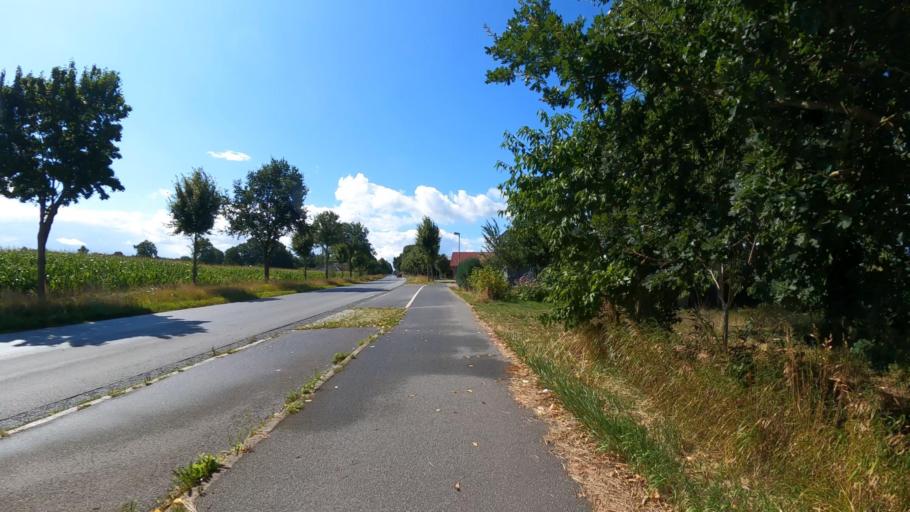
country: DE
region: Schleswig-Holstein
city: Wiemersdorf
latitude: 53.9531
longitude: 9.9012
